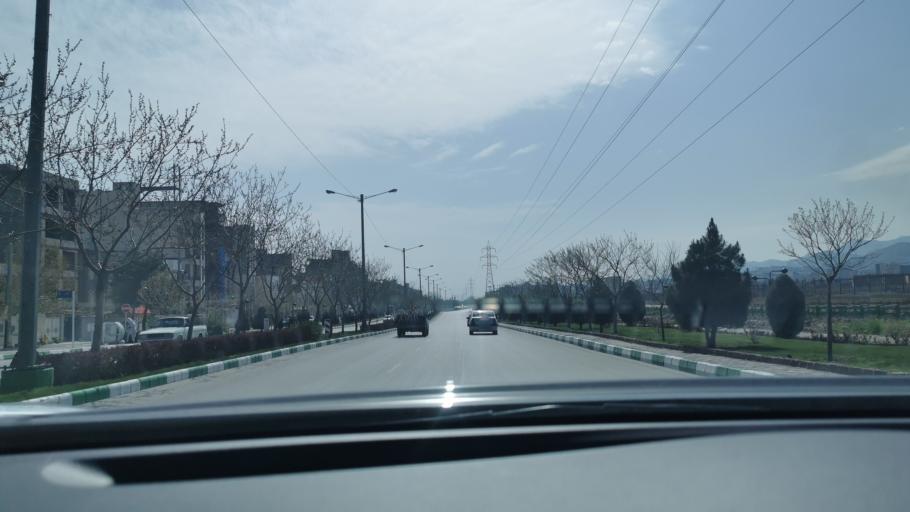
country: IR
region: Razavi Khorasan
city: Mashhad
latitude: 36.2867
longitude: 59.5373
